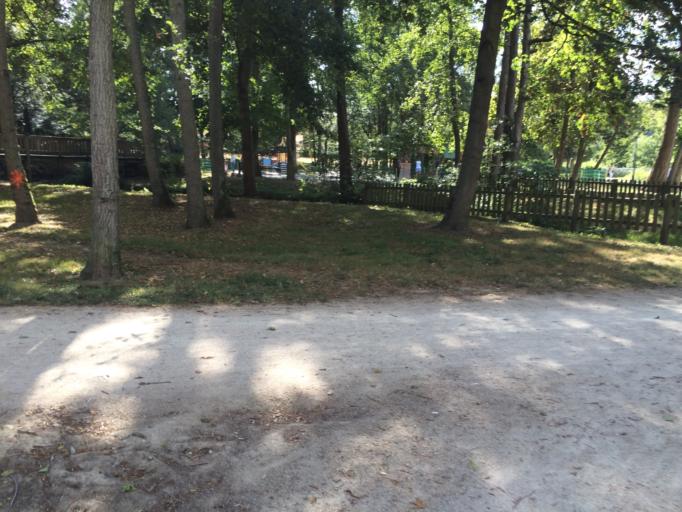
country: FR
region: Ile-de-France
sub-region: Departement de l'Essonne
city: Villebon-sur-Yvette
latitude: 48.7017
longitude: 2.2278
